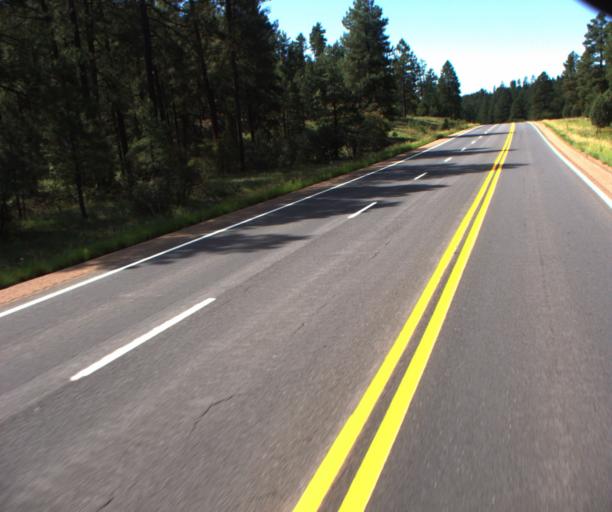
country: US
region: Arizona
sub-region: Navajo County
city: Show Low
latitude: 34.1809
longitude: -110.0950
